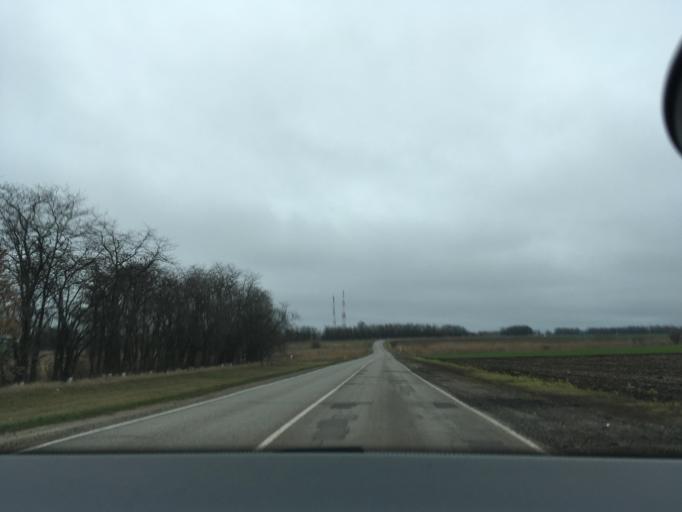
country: RU
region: Krasnodarskiy
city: Kushchevskaya
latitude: 46.5938
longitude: 39.6469
